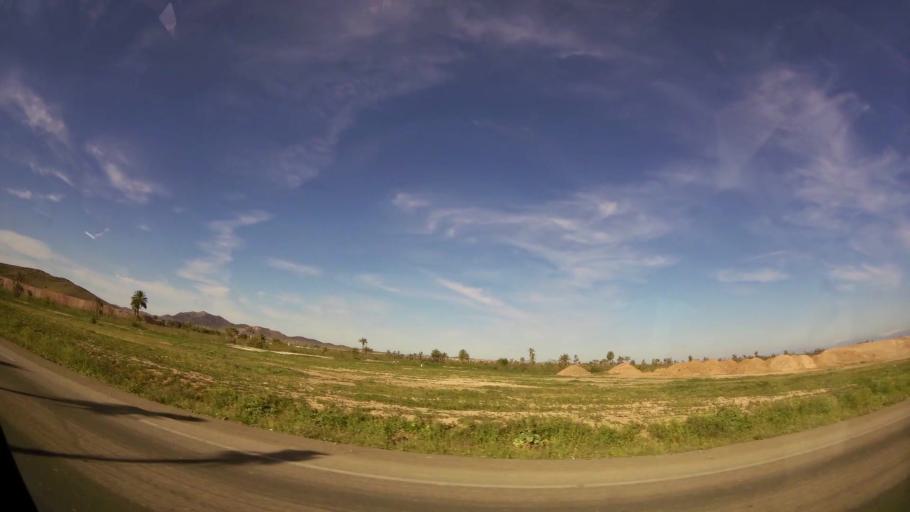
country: MA
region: Marrakech-Tensift-Al Haouz
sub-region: Marrakech
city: Marrakesh
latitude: 31.6974
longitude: -8.0590
